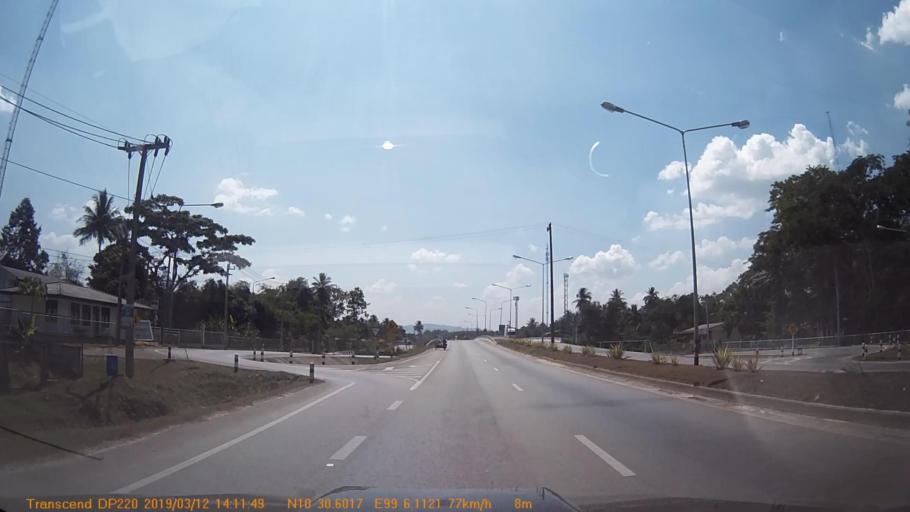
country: TH
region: Chumphon
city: Chumphon
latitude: 10.5100
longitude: 99.1017
